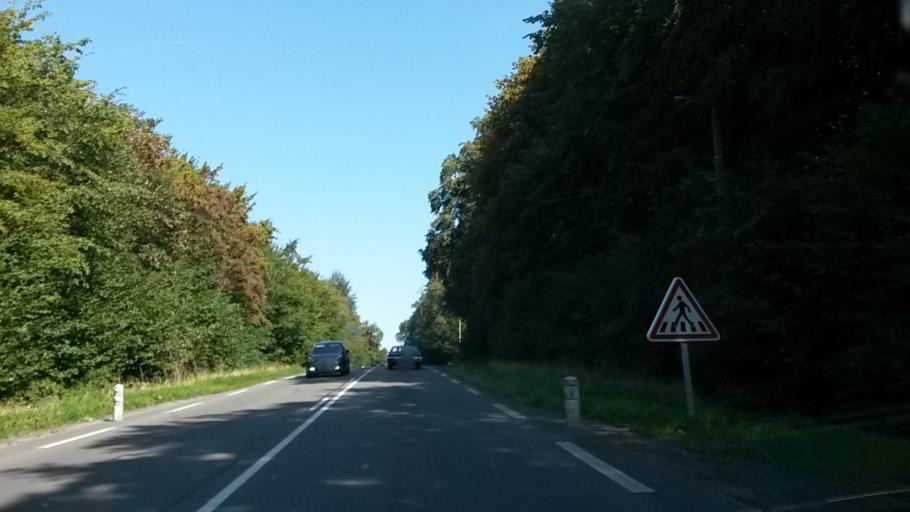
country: FR
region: Nord-Pas-de-Calais
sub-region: Departement du Nord
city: Hautmont
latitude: 50.1943
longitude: 3.9510
